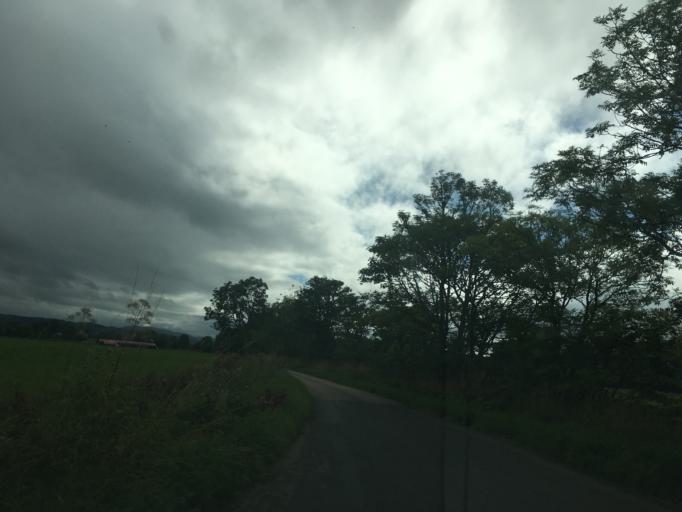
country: GB
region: Scotland
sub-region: Argyll and Bute
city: Lochgilphead
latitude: 56.1210
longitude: -5.4945
